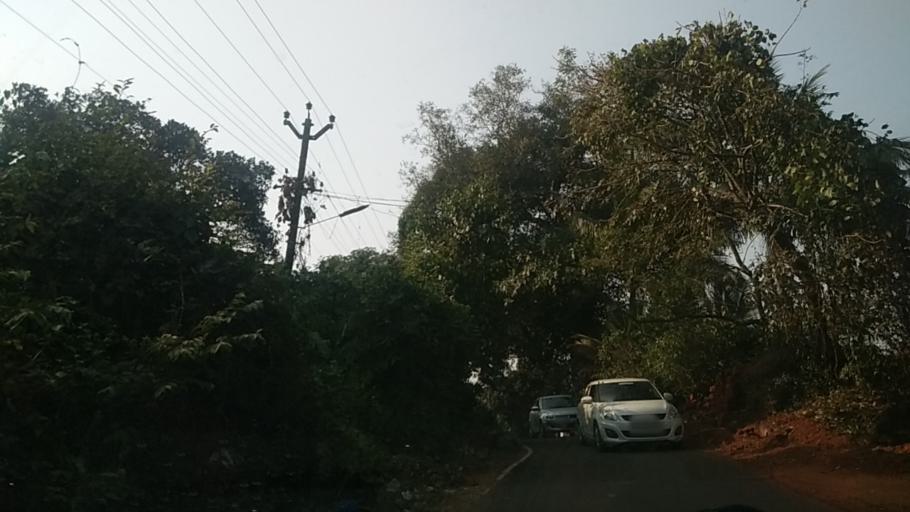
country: IN
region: Goa
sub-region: North Goa
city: Pernem
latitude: 15.7298
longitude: 73.7690
